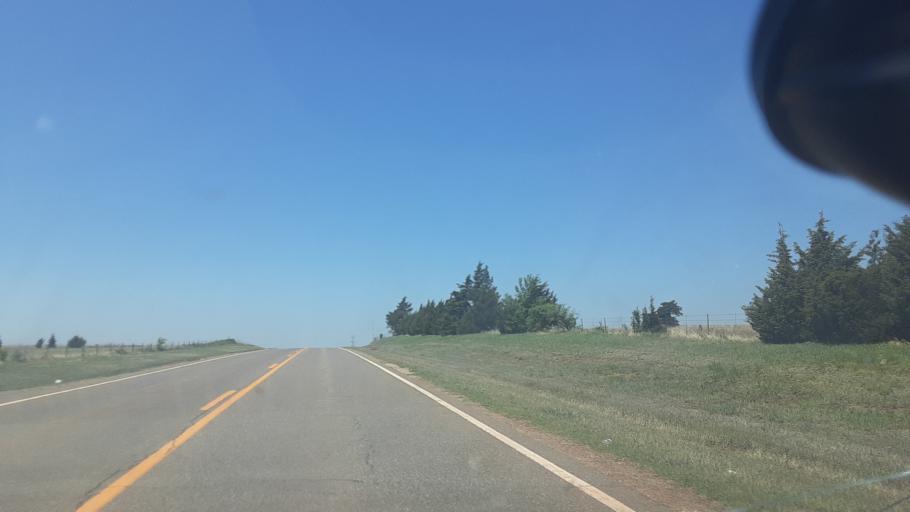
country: US
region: Oklahoma
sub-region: Noble County
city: Perry
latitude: 36.1157
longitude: -97.3608
